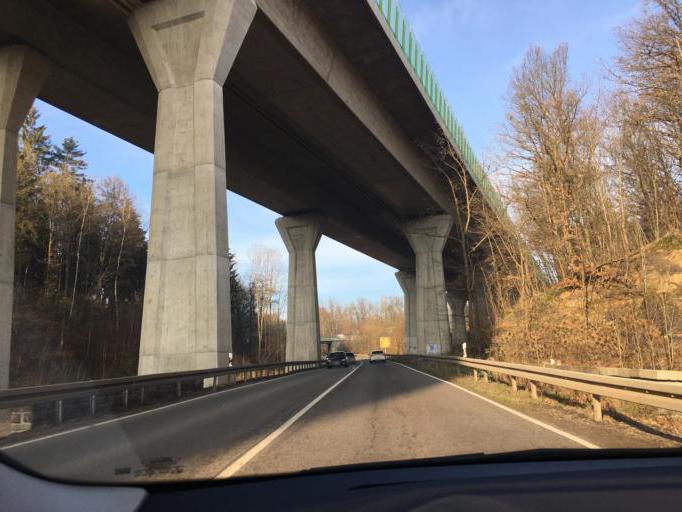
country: DE
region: Saxony
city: Penig
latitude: 50.9310
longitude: 12.6889
